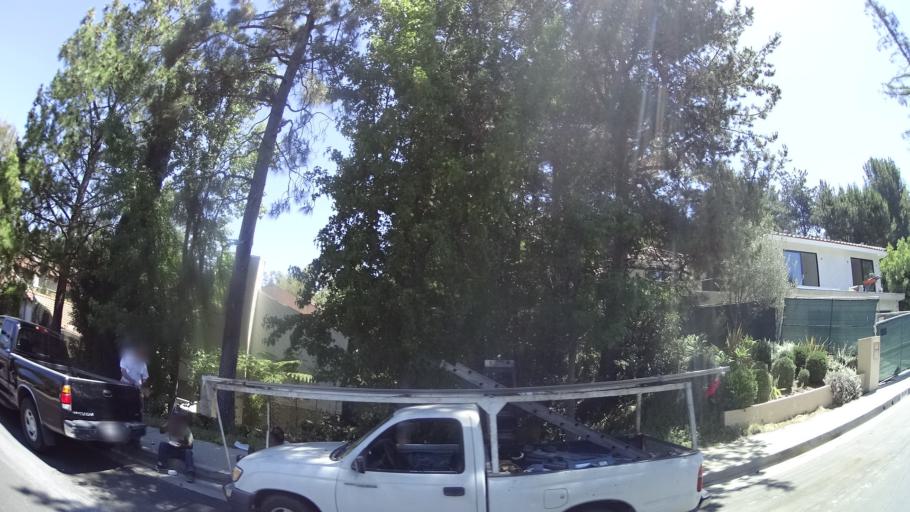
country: US
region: California
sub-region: Los Angeles County
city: Sherman Oaks
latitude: 34.1173
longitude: -118.4444
